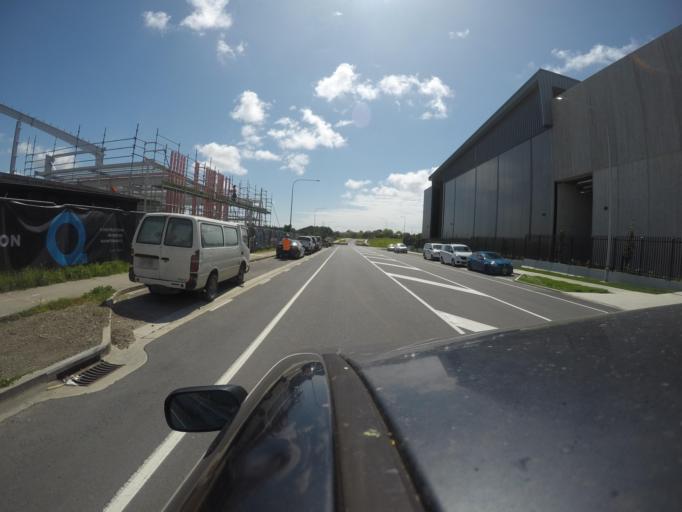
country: NZ
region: Auckland
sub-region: Auckland
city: Rosebank
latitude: -36.8030
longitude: 174.6359
